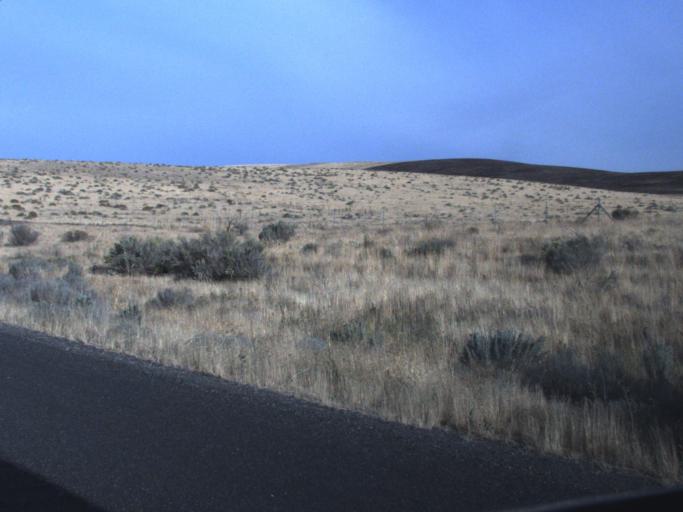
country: US
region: Oregon
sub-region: Umatilla County
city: Umatilla
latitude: 46.0011
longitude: -119.2548
